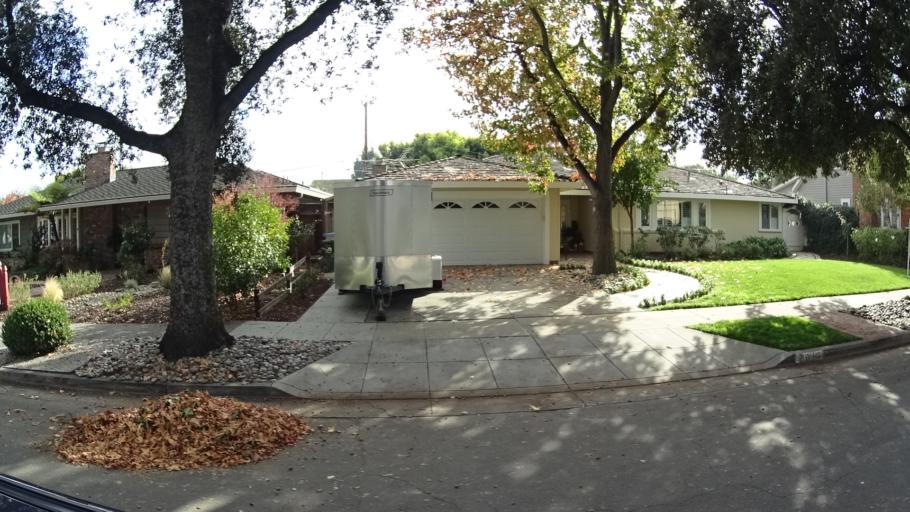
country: US
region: California
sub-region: Santa Clara County
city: Burbank
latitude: 37.3291
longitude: -121.9347
